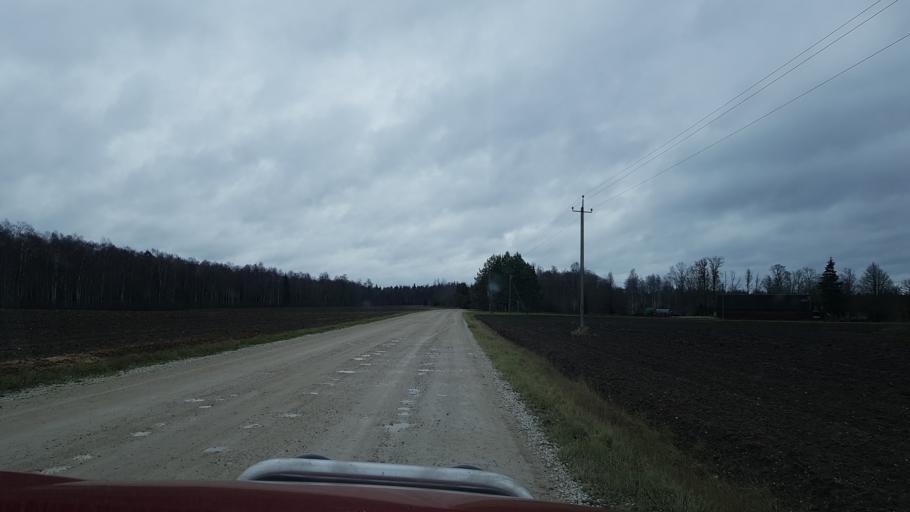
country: EE
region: Paernumaa
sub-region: Halinga vald
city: Parnu-Jaagupi
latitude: 58.5637
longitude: 24.4121
